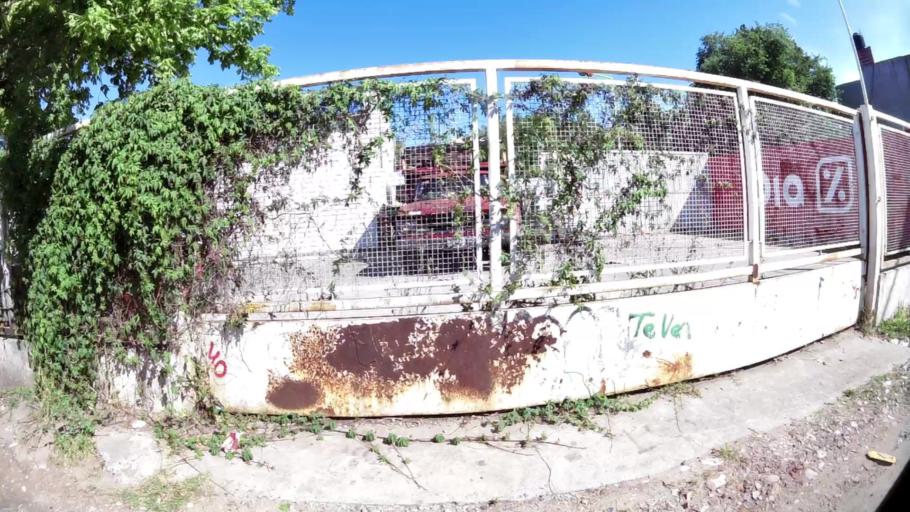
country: AR
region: Buenos Aires
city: Ituzaingo
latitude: -34.6277
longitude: -58.6561
